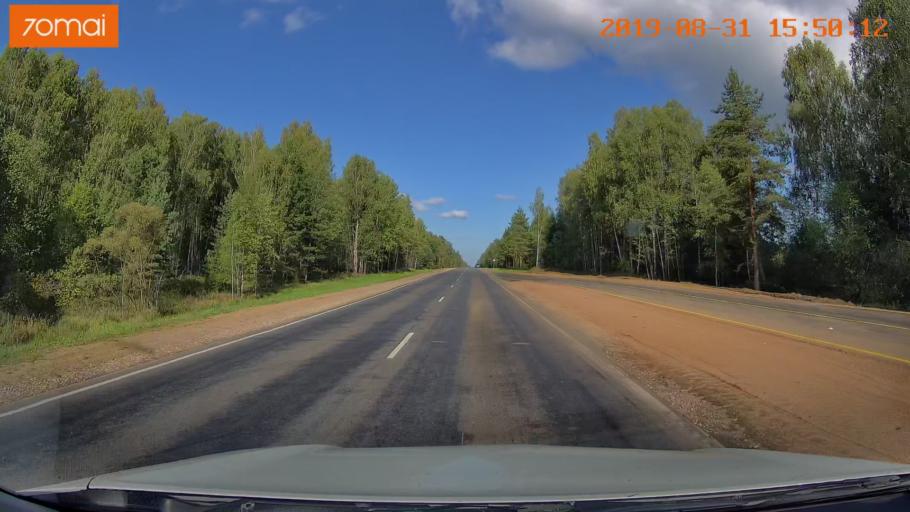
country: RU
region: Kaluga
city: Yukhnov
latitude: 54.6957
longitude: 35.0678
